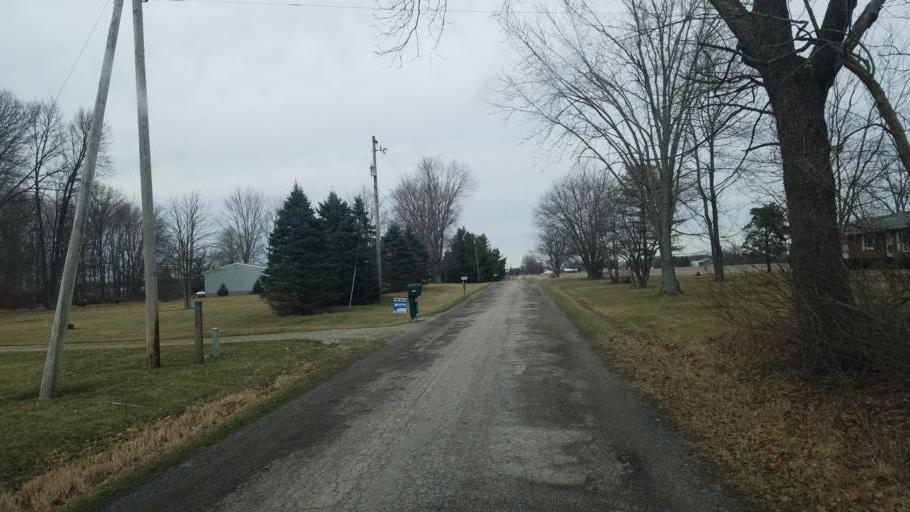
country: US
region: Ohio
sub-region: Morrow County
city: Cardington
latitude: 40.4600
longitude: -82.9309
